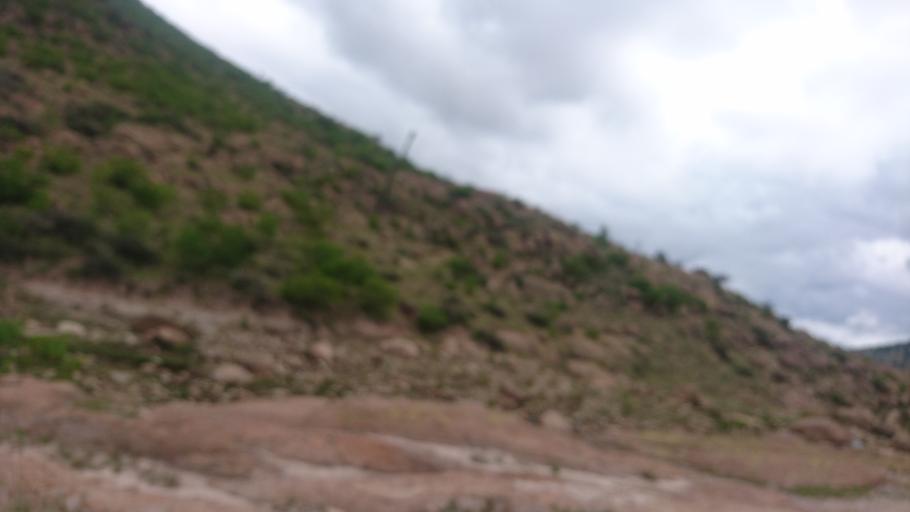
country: MX
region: San Luis Potosi
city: Escalerillas
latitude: 22.0742
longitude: -101.0939
